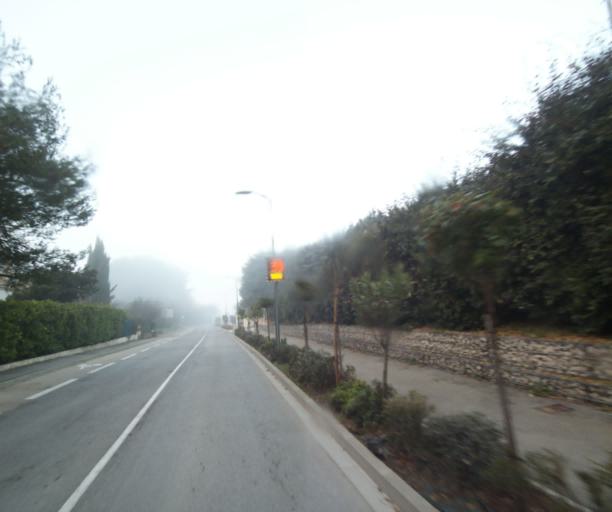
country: FR
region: Provence-Alpes-Cote d'Azur
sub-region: Departement des Bouches-du-Rhone
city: Meyreuil
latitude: 43.4817
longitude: 5.4968
